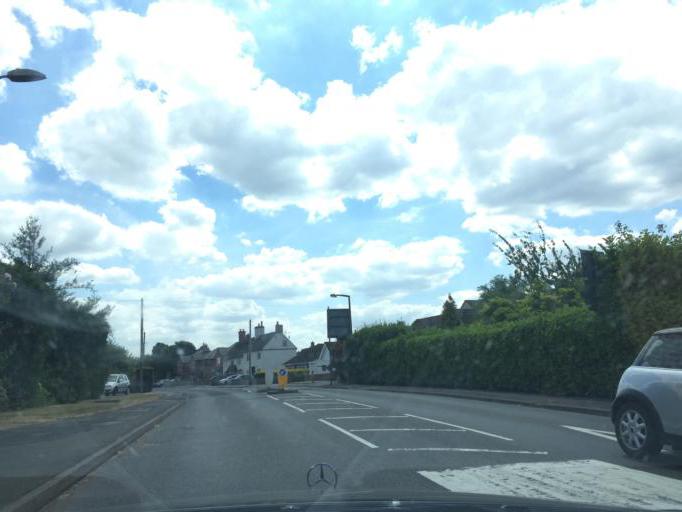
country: GB
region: England
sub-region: Leicestershire
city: Hinckley
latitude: 52.4867
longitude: -1.3692
